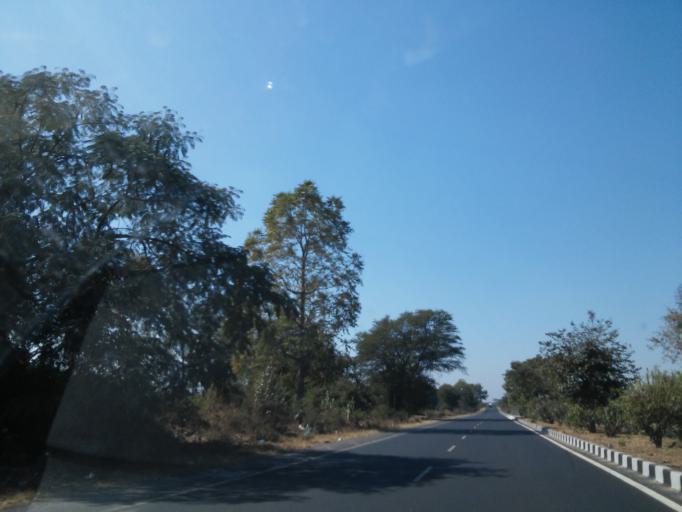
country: IN
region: Gujarat
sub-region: Sabar Kantha
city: Modasa
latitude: 23.6792
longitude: 73.3560
